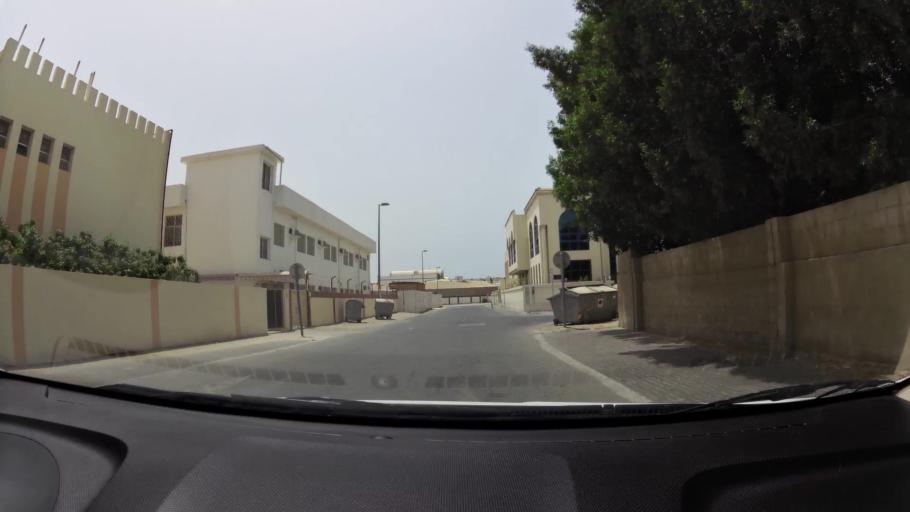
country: AE
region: Ash Shariqah
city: Sharjah
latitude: 25.3484
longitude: 55.4031
